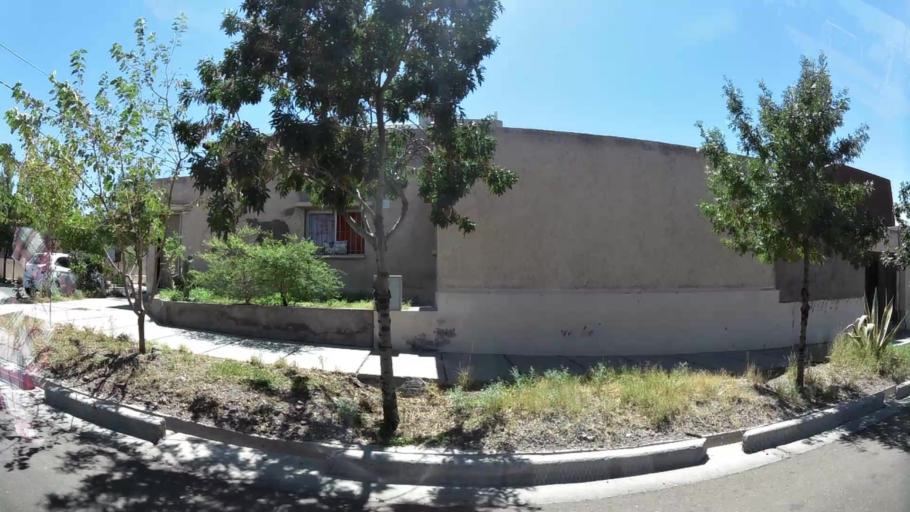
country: AR
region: Mendoza
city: Las Heras
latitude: -32.8496
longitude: -68.8610
